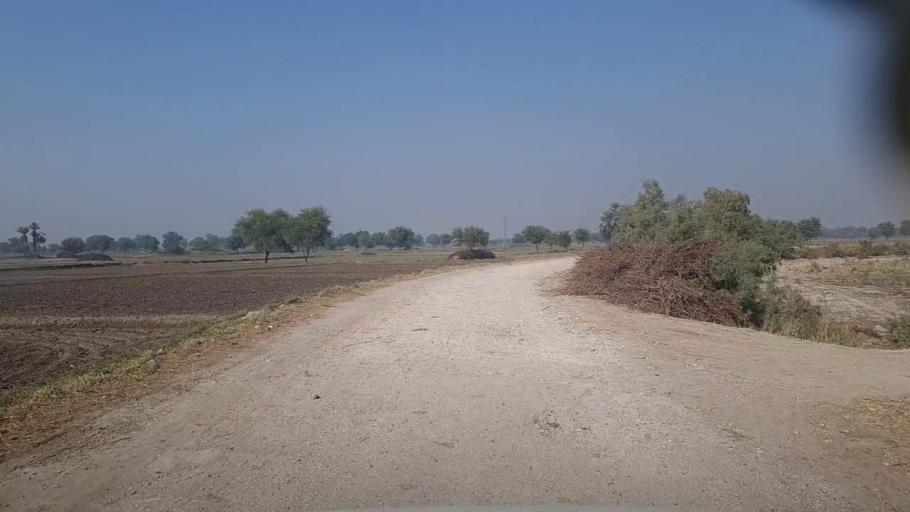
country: PK
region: Sindh
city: Kandiari
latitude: 26.9300
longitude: 68.5238
